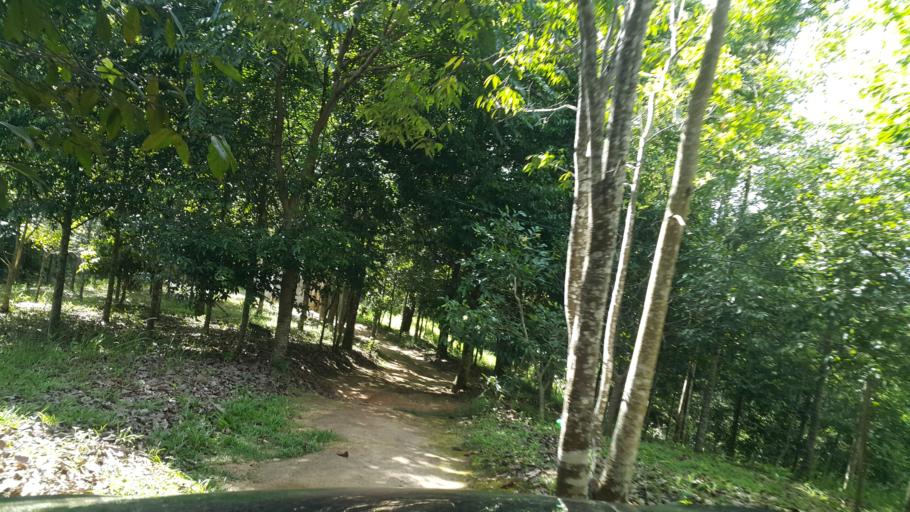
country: TH
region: Loei
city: Na Haeo
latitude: 17.5553
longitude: 100.9555
